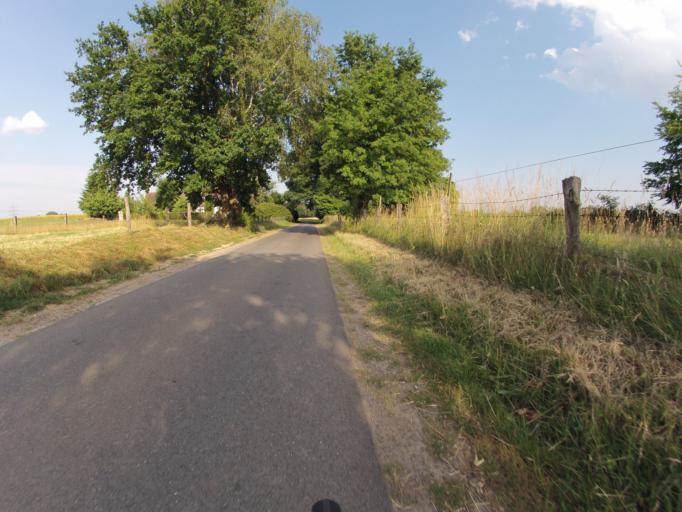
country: DE
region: North Rhine-Westphalia
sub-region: Regierungsbezirk Munster
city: Tecklenburg
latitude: 52.2714
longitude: 7.8349
